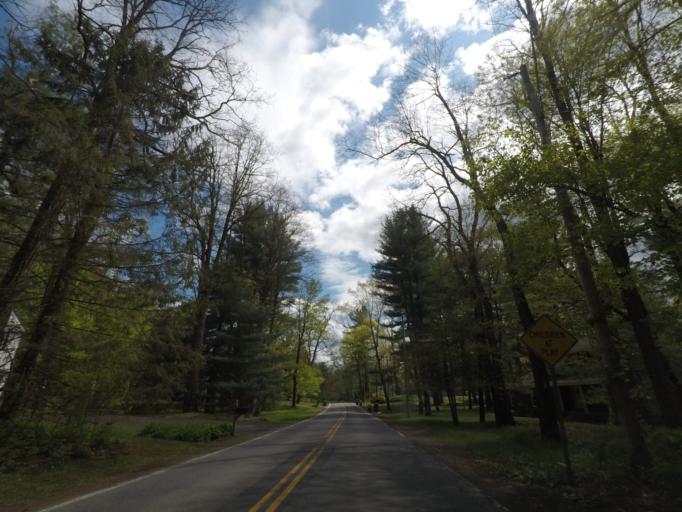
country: US
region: New York
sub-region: Albany County
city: Westmere
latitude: 42.7311
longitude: -73.9041
